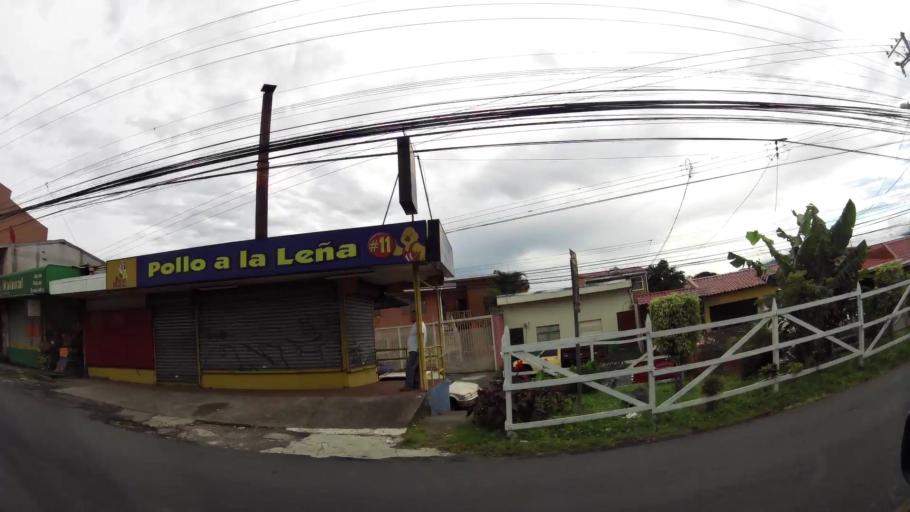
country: CR
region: San Jose
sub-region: Canton de Goicoechea
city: Guadalupe
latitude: 9.9554
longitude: -84.0549
